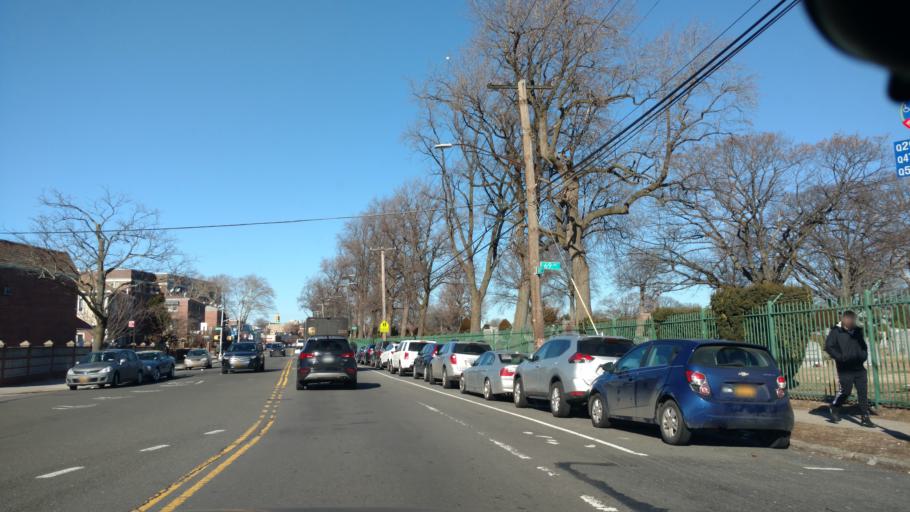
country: US
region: New York
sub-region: Queens County
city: Borough of Queens
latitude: 40.7098
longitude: -73.8702
